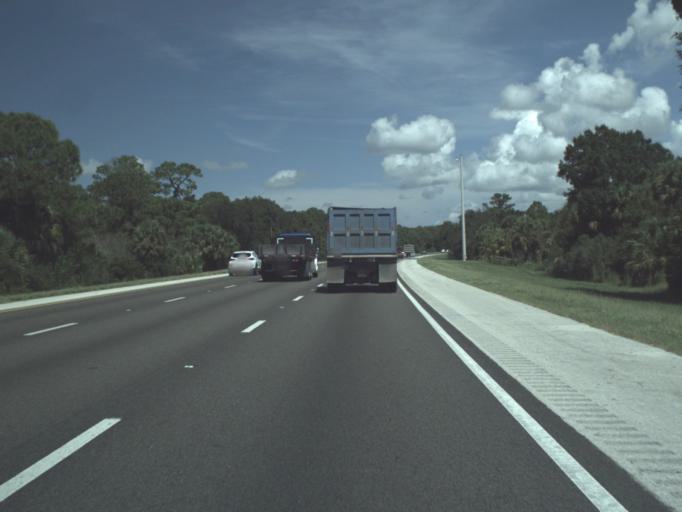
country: US
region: Florida
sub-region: Sarasota County
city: Vamo
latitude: 27.2251
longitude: -82.4501
